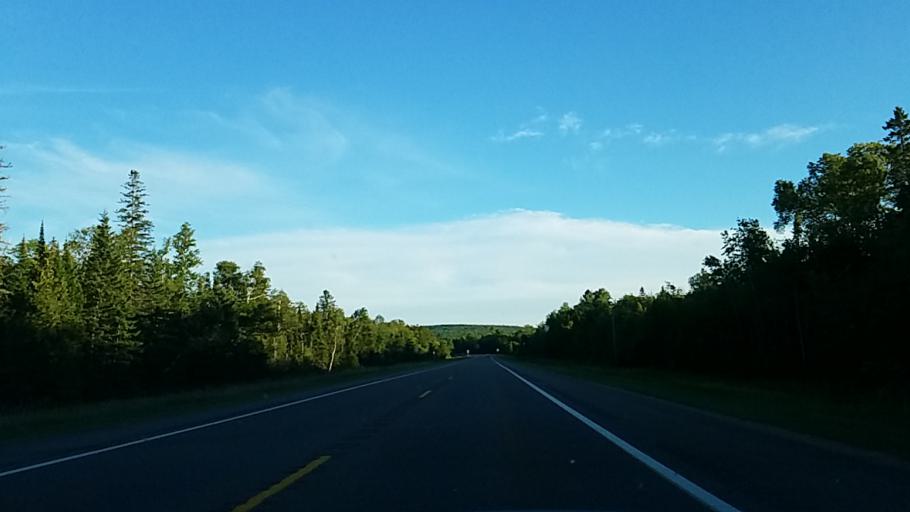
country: US
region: Michigan
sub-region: Alger County
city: Munising
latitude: 46.4484
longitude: -86.8880
